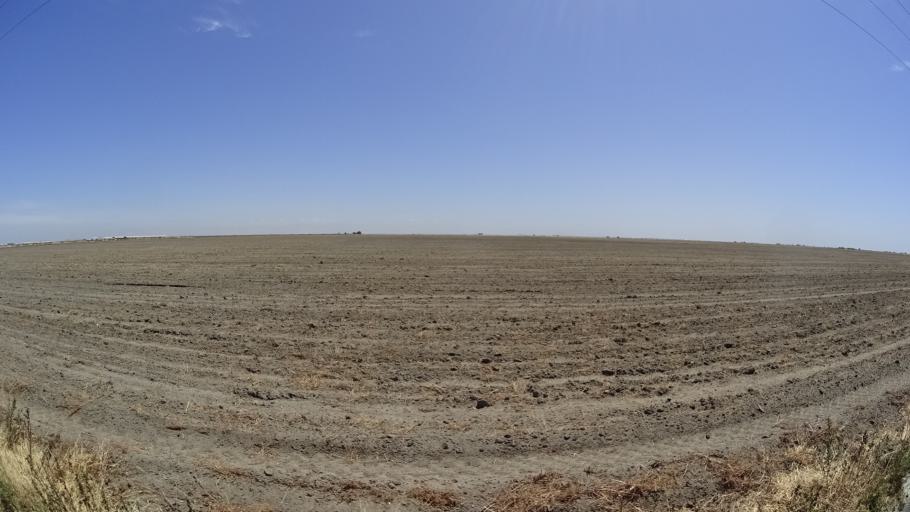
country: US
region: California
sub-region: Kings County
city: Stratford
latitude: 36.1503
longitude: -119.7173
